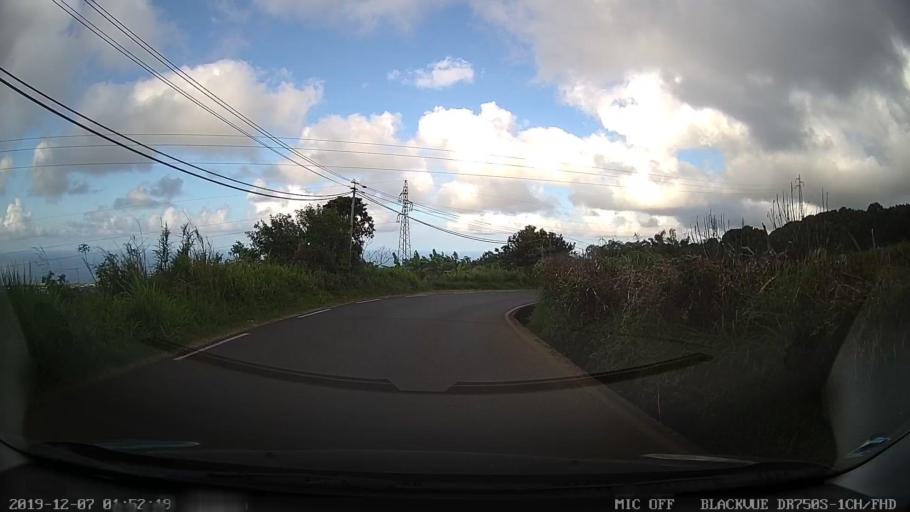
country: RE
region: Reunion
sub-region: Reunion
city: Sainte-Marie
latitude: -20.9398
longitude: 55.5342
